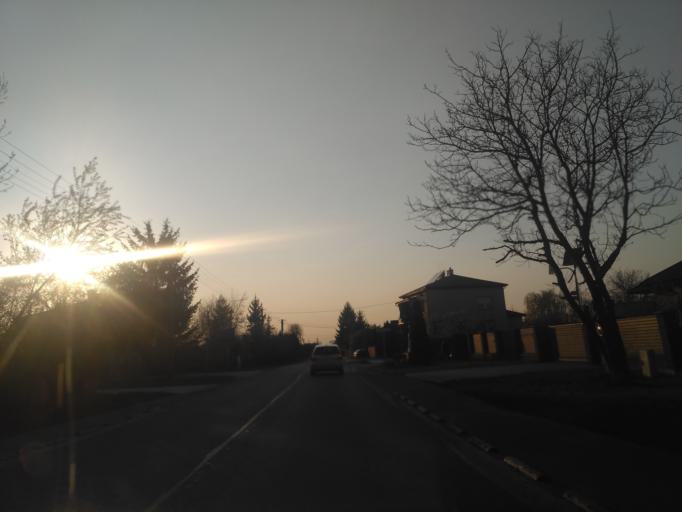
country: PL
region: Lublin Voivodeship
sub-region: Powiat chelmski
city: Pokrowka
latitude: 51.1001
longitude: 23.4806
